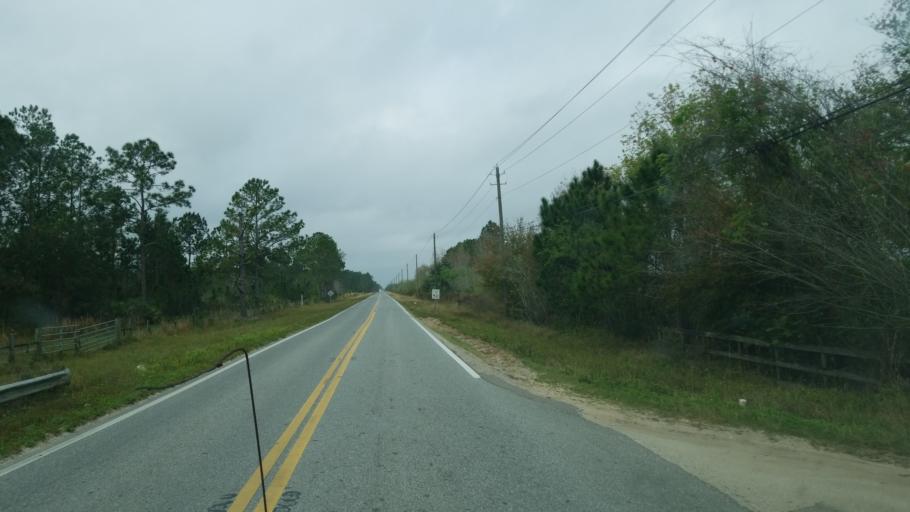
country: US
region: Florida
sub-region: Polk County
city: Polk City
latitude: 28.2591
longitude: -81.8779
